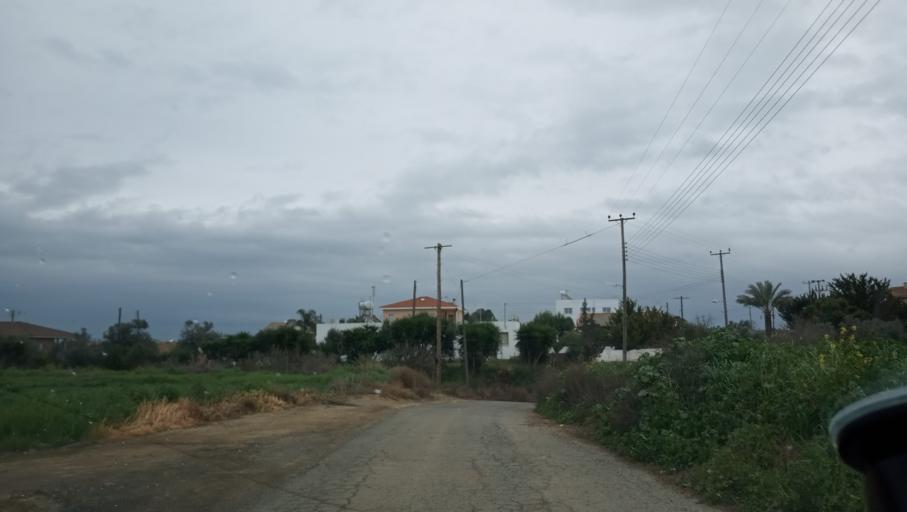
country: CY
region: Lefkosia
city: Kato Deftera
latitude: 35.0814
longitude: 33.2766
